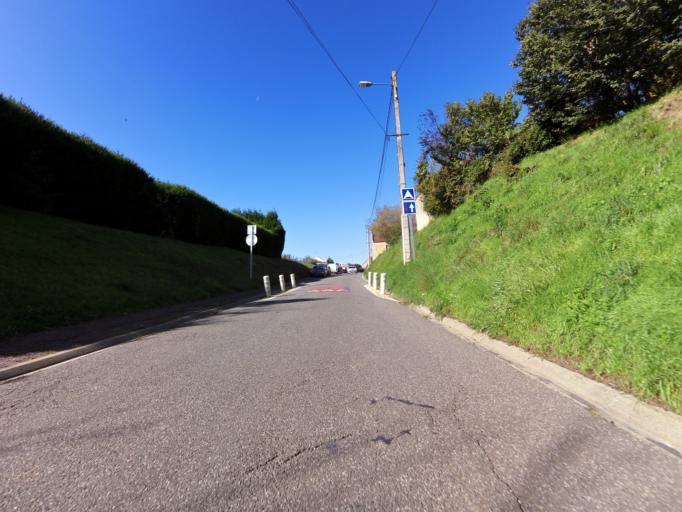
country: FR
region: Lower Normandy
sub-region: Departement du Calvados
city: Canon
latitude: 49.0467
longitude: -0.1273
